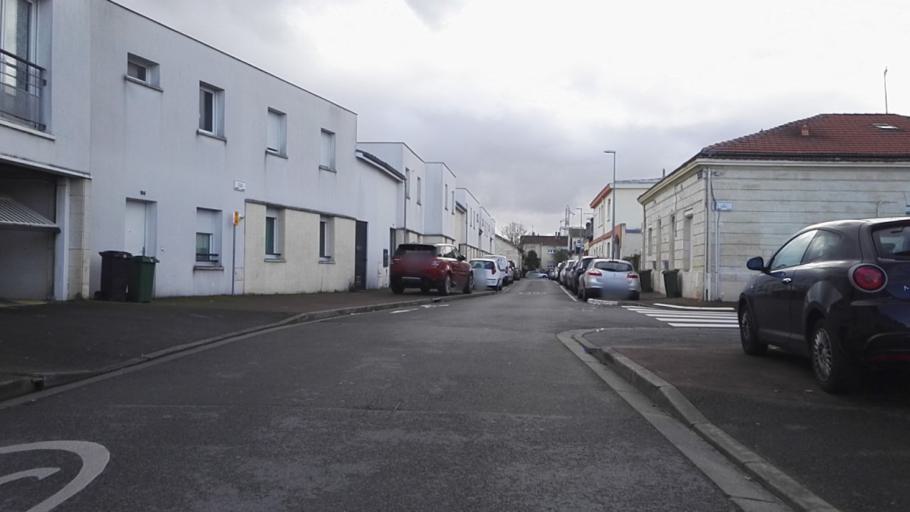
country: FR
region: Aquitaine
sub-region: Departement de la Gironde
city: Talence
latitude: 44.8180
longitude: -0.5963
